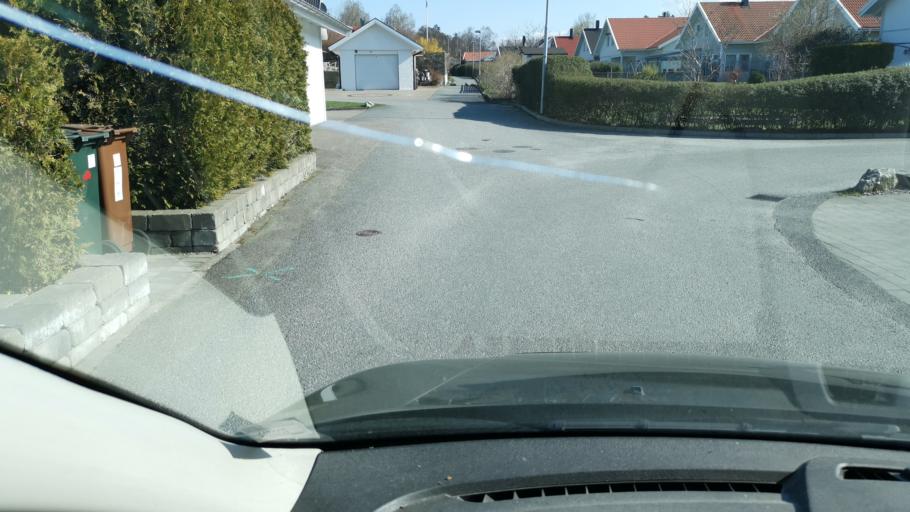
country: SE
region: Vaestra Goetaland
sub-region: Goteborg
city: Torslanda
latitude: 57.7433
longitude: 11.8294
